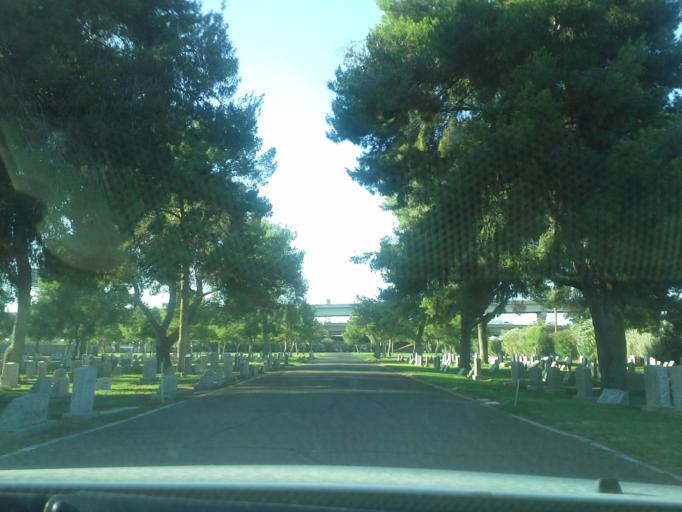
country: US
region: Arizona
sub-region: Maricopa County
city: Phoenix
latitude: 33.4595
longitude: -112.1123
